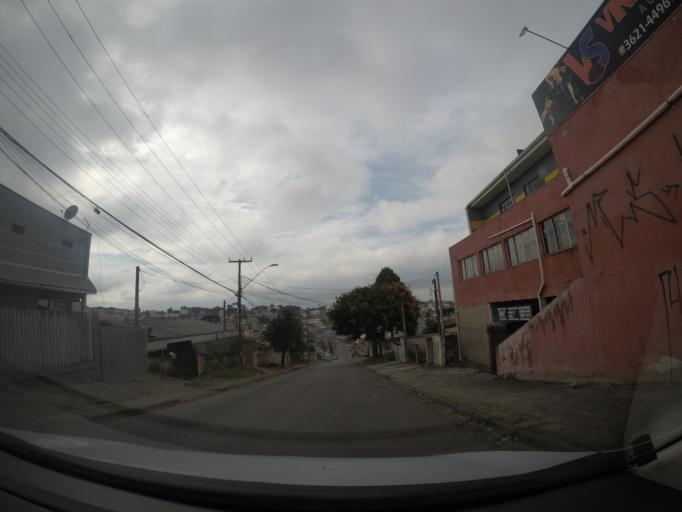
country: BR
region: Parana
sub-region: Colombo
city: Colombo
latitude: -25.3542
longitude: -49.2073
